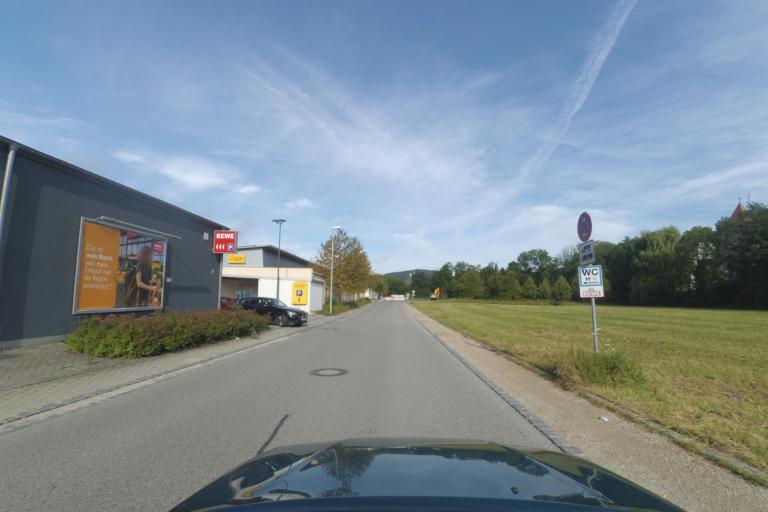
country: DE
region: Bavaria
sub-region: Lower Bavaria
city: Riedenburg
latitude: 48.9586
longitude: 11.6993
